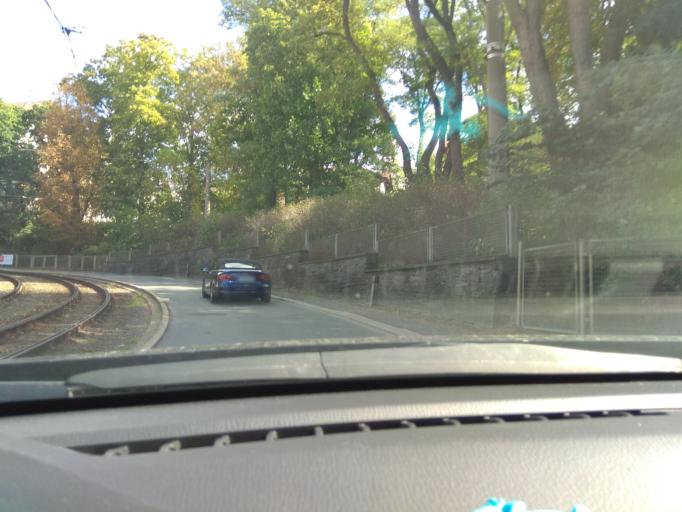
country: DE
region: Saxony
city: Plauen
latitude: 50.4916
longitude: 12.1504
